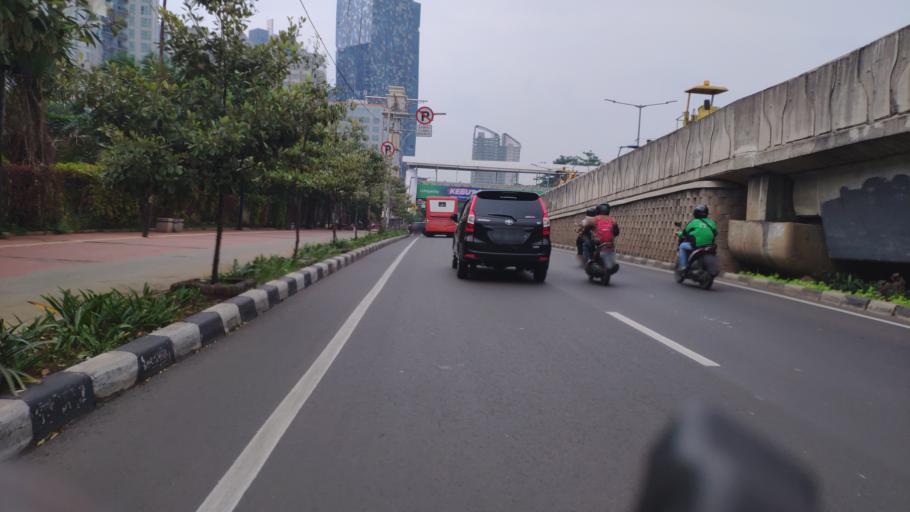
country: ID
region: Jakarta Raya
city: Jakarta
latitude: -6.2253
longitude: 106.8374
